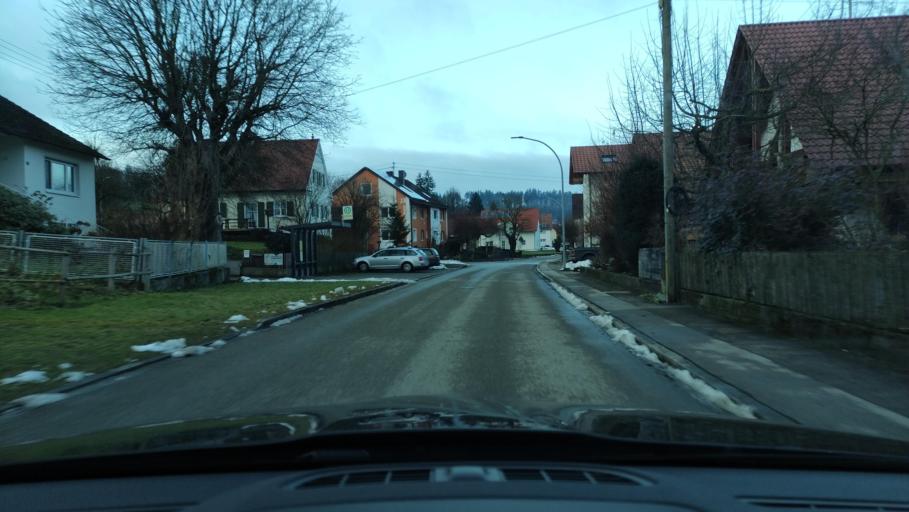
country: DE
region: Bavaria
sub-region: Swabia
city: Deisenhausen
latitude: 48.2930
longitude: 10.3565
